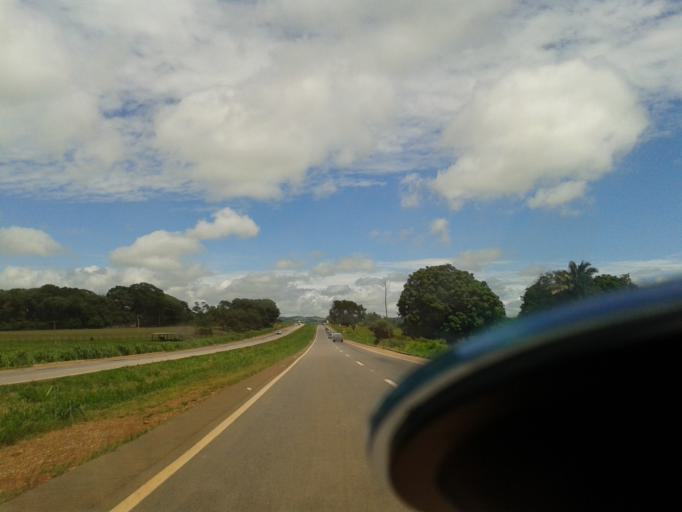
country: BR
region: Goias
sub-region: Inhumas
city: Inhumas
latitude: -16.2494
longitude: -49.5530
